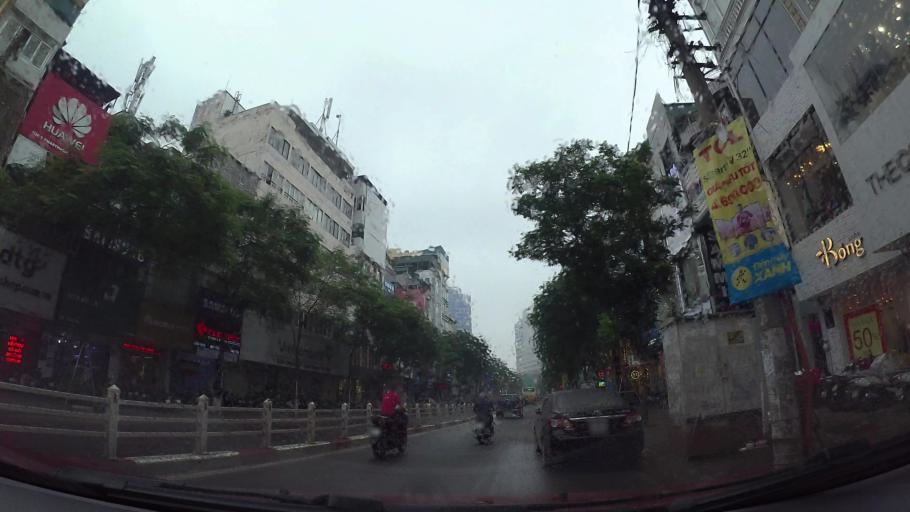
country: VN
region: Ha Noi
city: Dong Da
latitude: 21.0119
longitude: 105.8213
